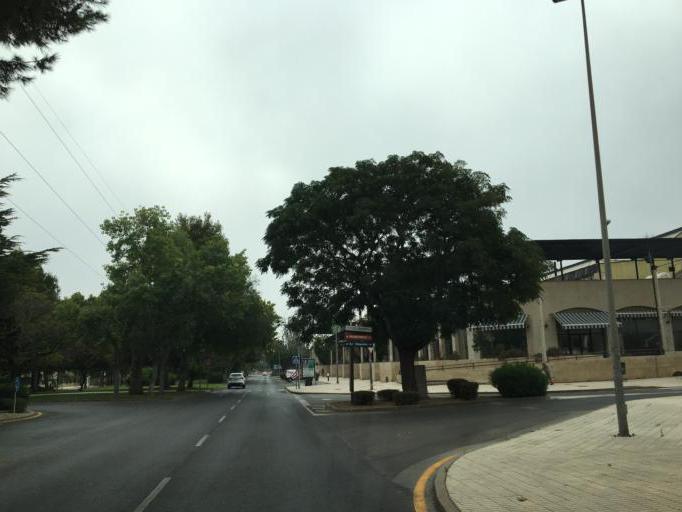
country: ES
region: Murcia
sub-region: Murcia
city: Cartagena
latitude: 37.6521
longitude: -1.0107
